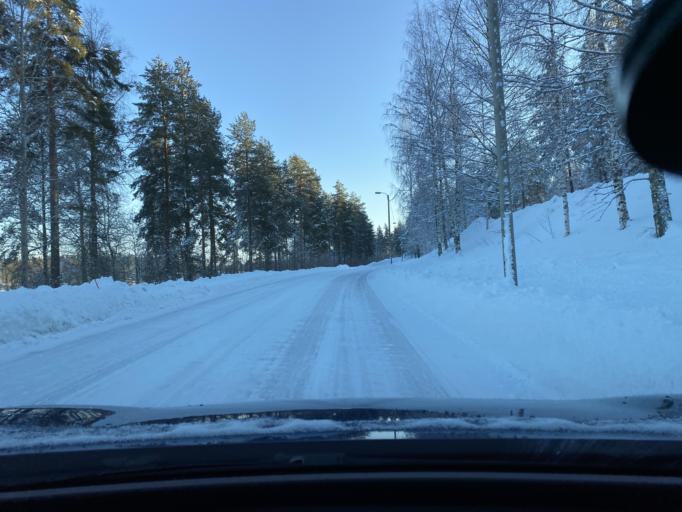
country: FI
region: Southern Savonia
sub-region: Mikkeli
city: Kangasniemi
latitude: 62.0115
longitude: 26.6197
